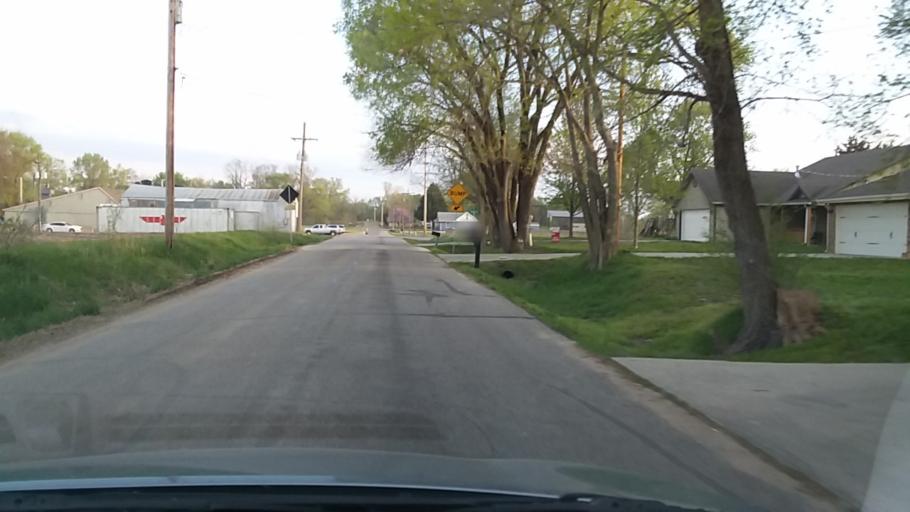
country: US
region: Kansas
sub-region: Douglas County
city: Lawrence
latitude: 38.9760
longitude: -95.2144
